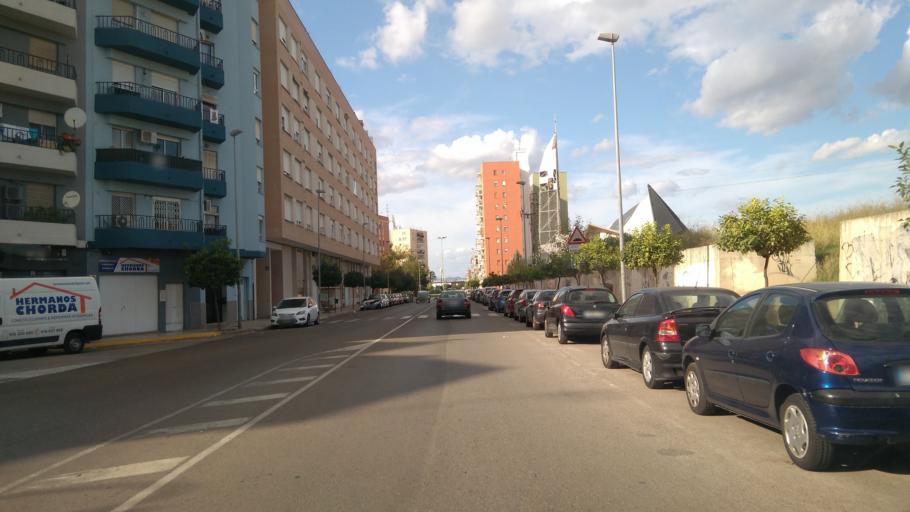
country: ES
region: Valencia
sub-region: Provincia de Valencia
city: Alzira
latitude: 39.1556
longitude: -0.4275
